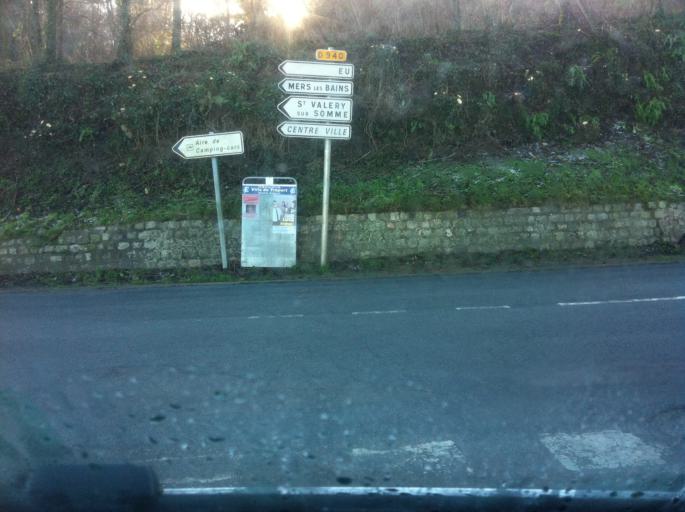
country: FR
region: Haute-Normandie
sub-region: Departement de la Seine-Maritime
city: Le Treport
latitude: 50.0541
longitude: 1.3703
